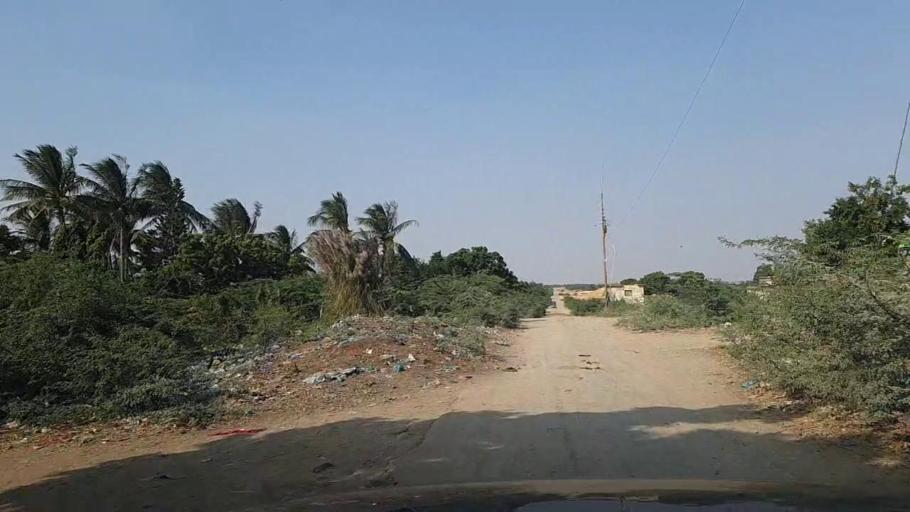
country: PK
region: Sindh
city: Gharo
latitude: 24.7536
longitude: 67.5807
